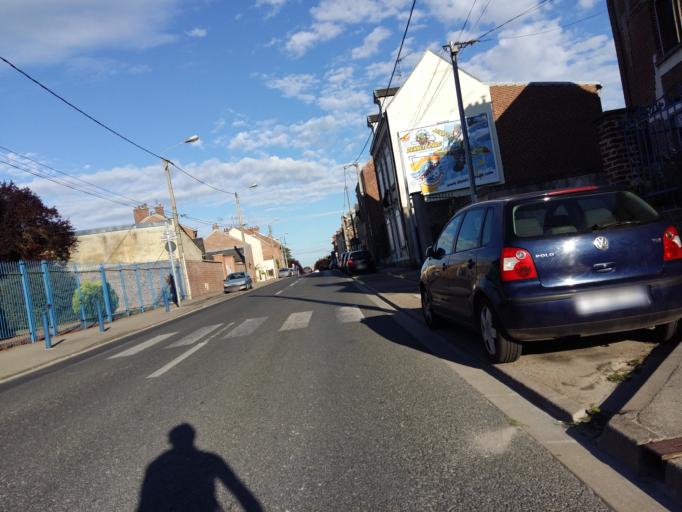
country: FR
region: Picardie
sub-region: Departement de la Somme
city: Rivery
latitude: 49.9022
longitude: 2.3249
